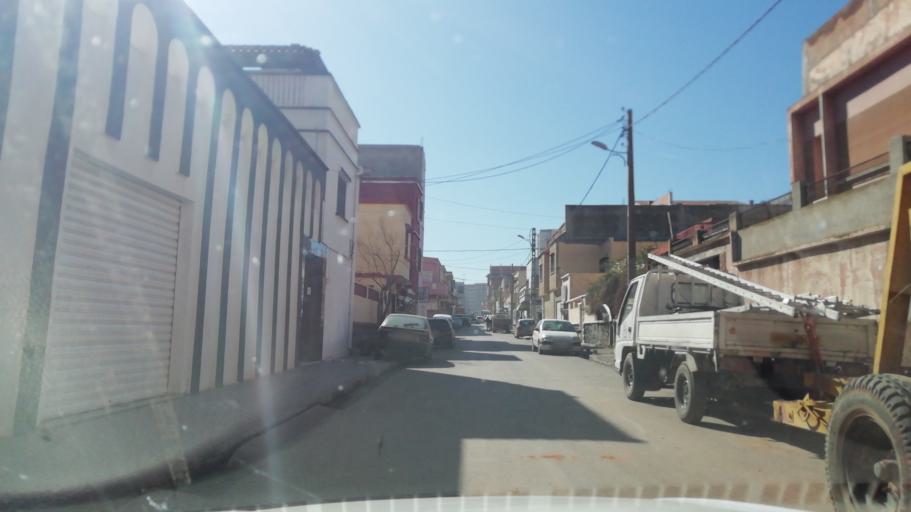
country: DZ
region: Oran
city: Oran
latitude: 35.6940
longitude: -0.6211
